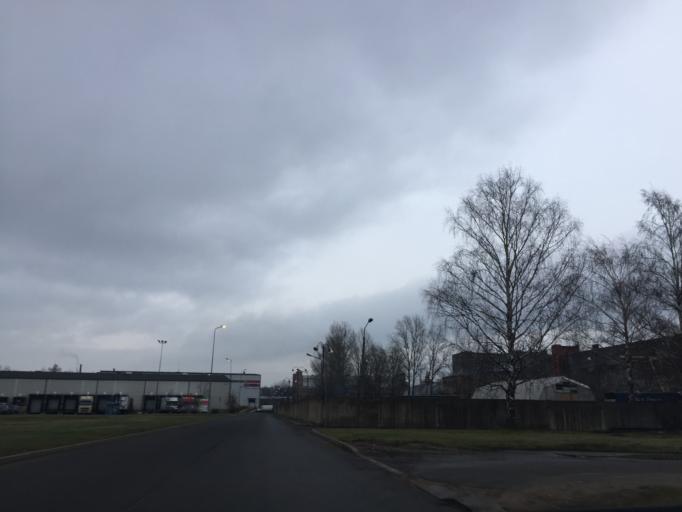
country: LV
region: Riga
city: Riga
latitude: 56.9912
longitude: 24.1130
